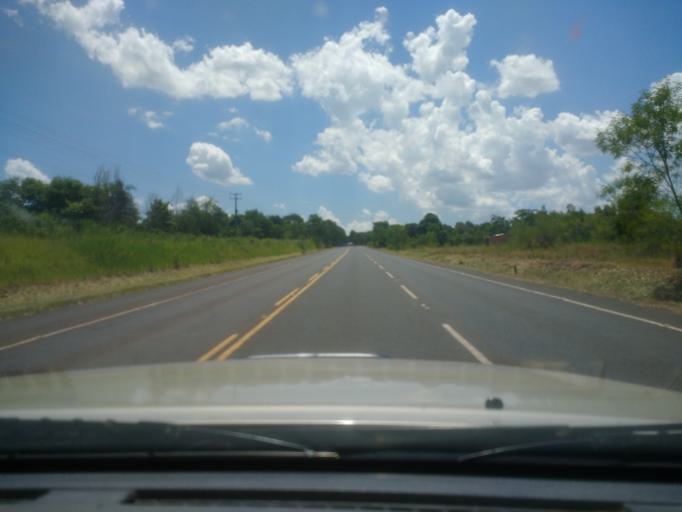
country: PY
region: San Pedro
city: Guayaybi
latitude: -24.5977
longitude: -56.5056
